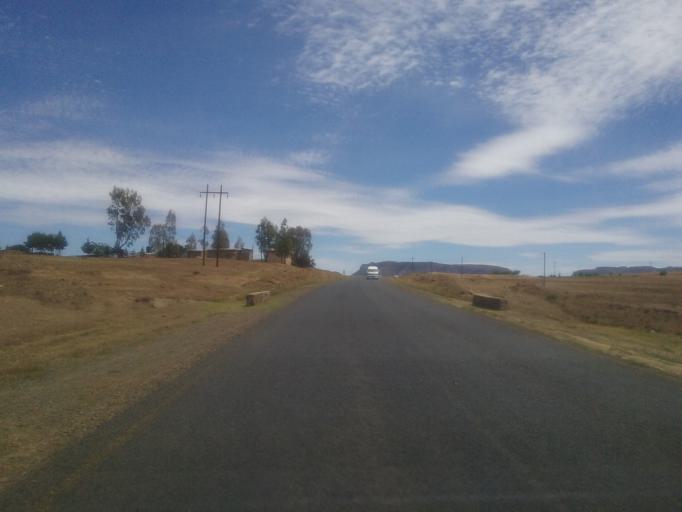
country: LS
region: Mafeteng
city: Mafeteng
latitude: -29.9827
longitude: 27.3243
